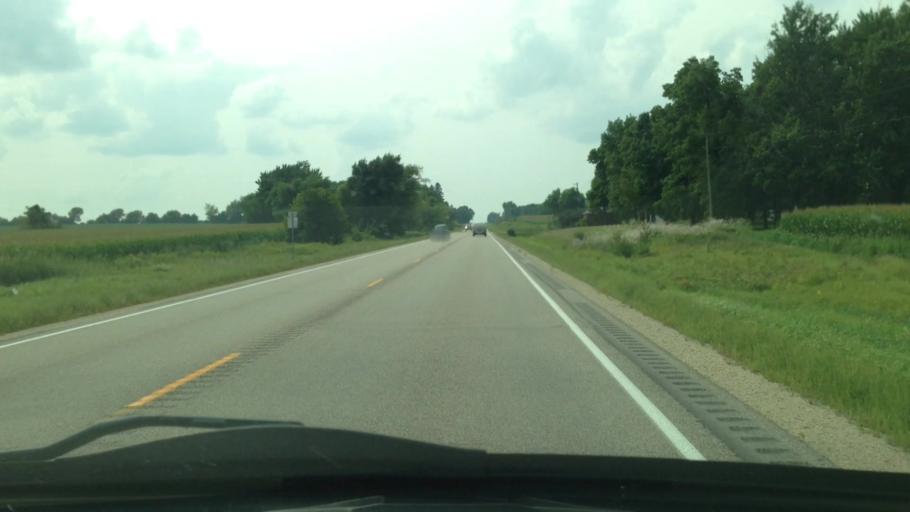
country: US
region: Minnesota
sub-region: Wabasha County
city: Elgin
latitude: 44.1658
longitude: -92.3815
